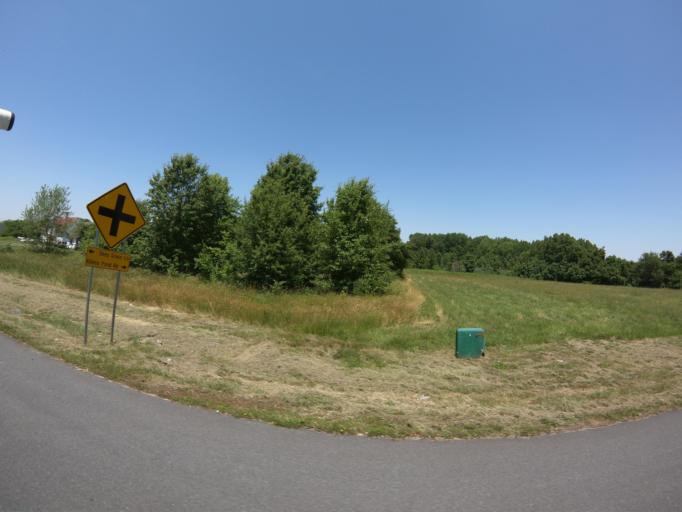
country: US
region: Delaware
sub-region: Kent County
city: Harrington
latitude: 38.9277
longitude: -75.5151
